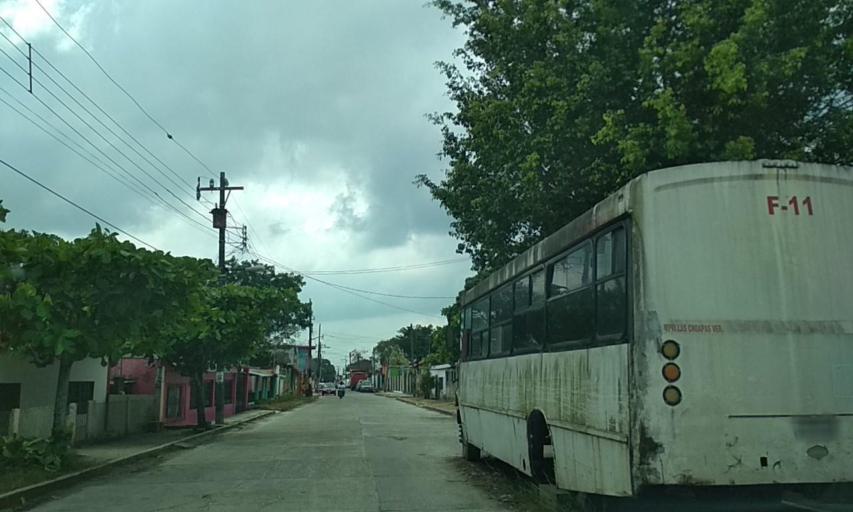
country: MX
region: Veracruz
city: Las Choapas
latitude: 17.8993
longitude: -94.1029
